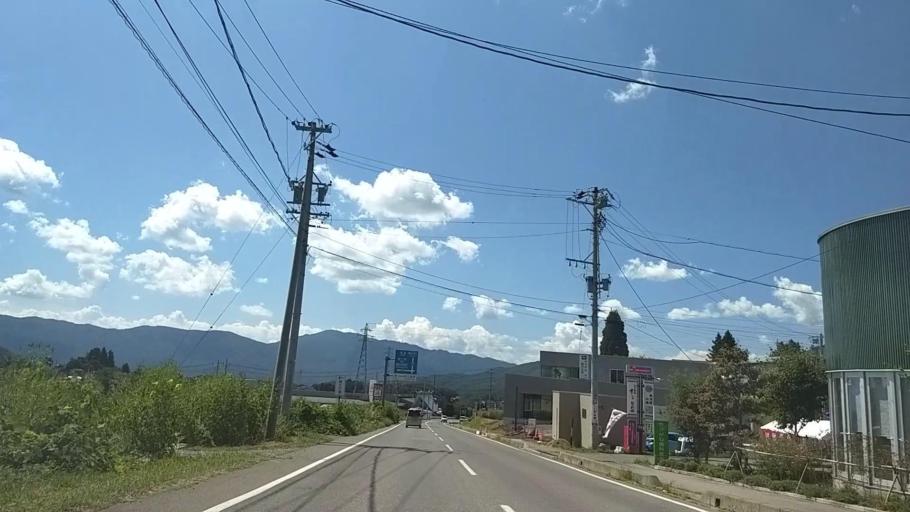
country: JP
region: Nagano
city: Chino
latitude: 36.0217
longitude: 138.2071
